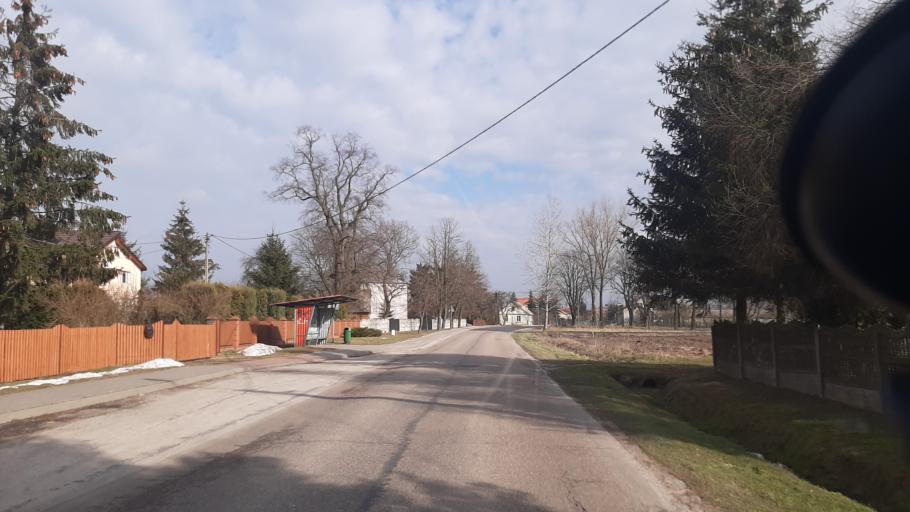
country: PL
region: Lublin Voivodeship
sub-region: Powiat lubartowski
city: Wola Sernicka
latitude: 51.4663
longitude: 22.7270
